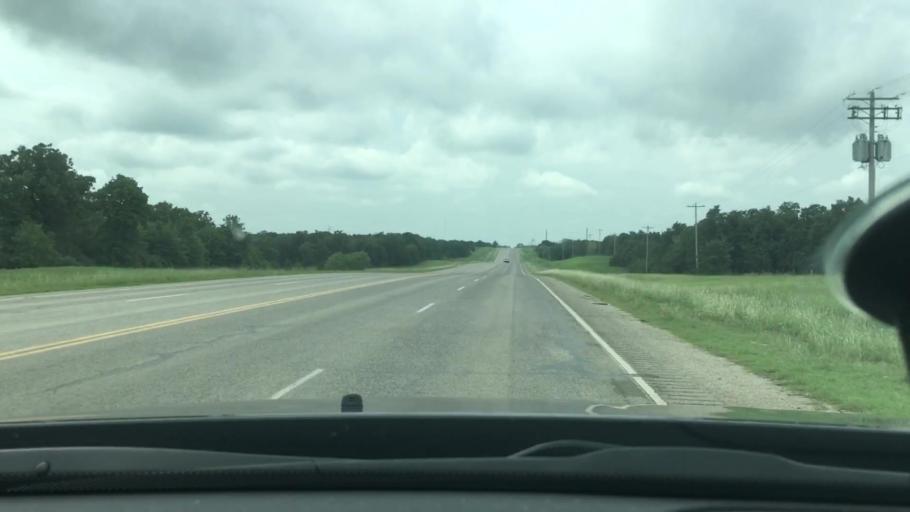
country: US
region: Oklahoma
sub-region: Carter County
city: Healdton
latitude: 34.1873
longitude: -97.4749
